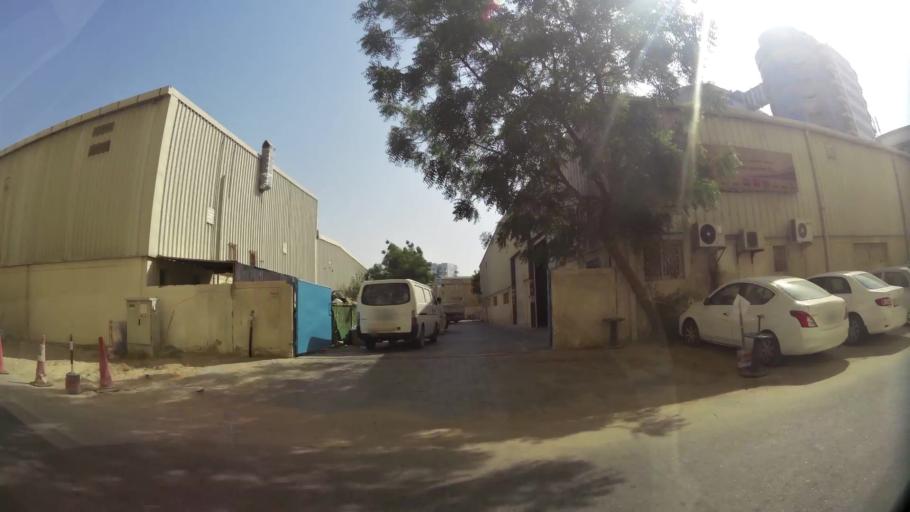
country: AE
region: Ash Shariqah
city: Sharjah
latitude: 25.2934
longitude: 55.3941
